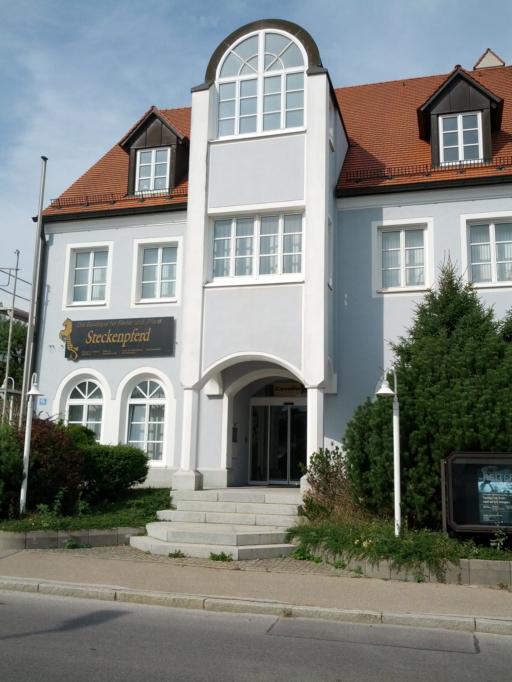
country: DE
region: Bavaria
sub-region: Upper Bavaria
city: Pfaffenhofen an der Ilm
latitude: 48.5337
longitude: 11.4939
